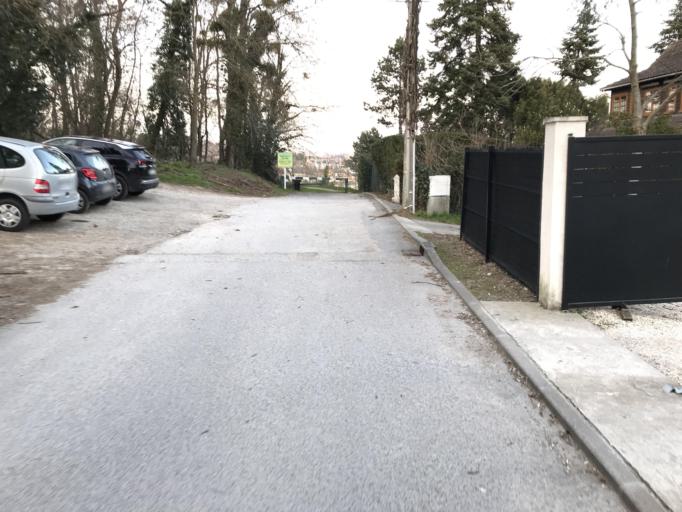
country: FR
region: Ile-de-France
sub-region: Departement de l'Essonne
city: La Ville-du-Bois
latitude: 48.6651
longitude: 2.2742
